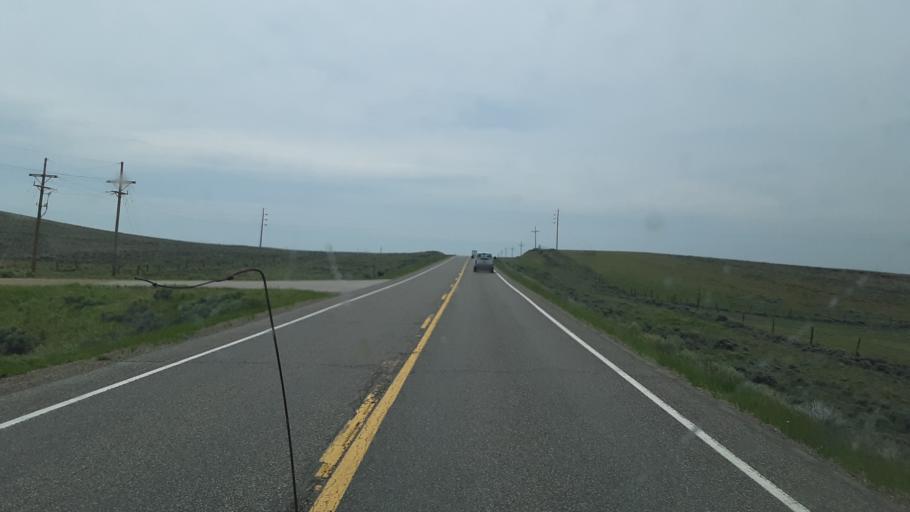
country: US
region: Colorado
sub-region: Jackson County
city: Walden
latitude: 40.8119
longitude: -106.2917
